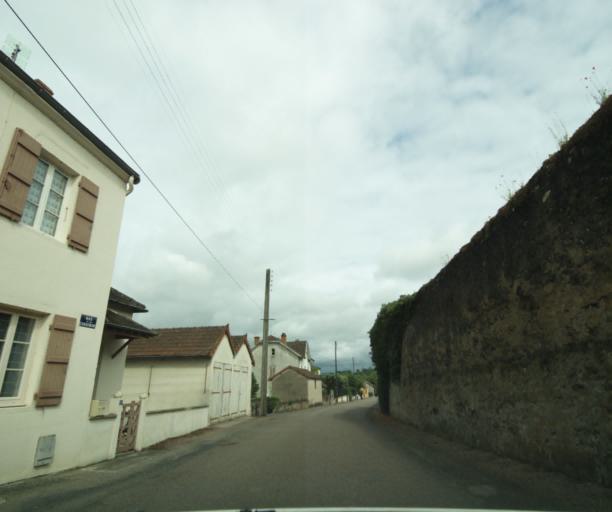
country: FR
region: Bourgogne
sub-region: Departement de Saone-et-Loire
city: Charolles
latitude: 46.4338
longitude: 4.2806
